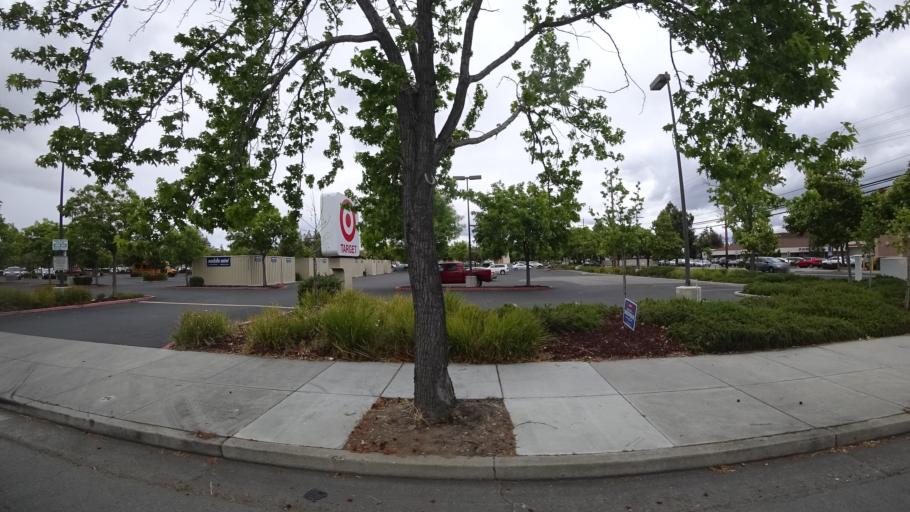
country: US
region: California
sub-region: Santa Clara County
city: Cambrian Park
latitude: 37.2636
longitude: -121.9170
